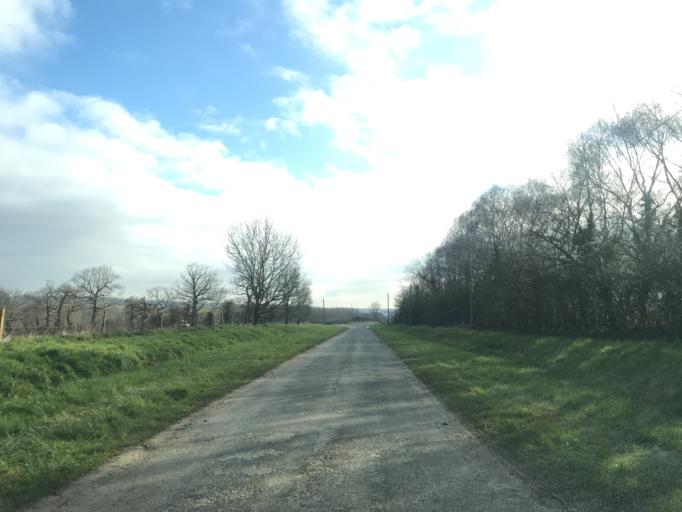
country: FR
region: Lower Normandy
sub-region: Departement du Calvados
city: Dives-sur-Mer
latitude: 49.2226
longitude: -0.1083
